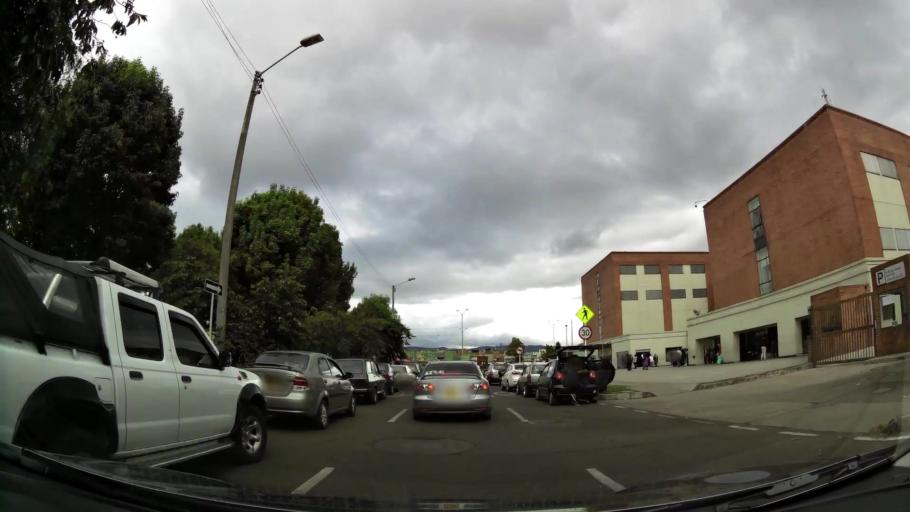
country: CO
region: Cundinamarca
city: Cota
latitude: 4.7116
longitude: -74.1102
